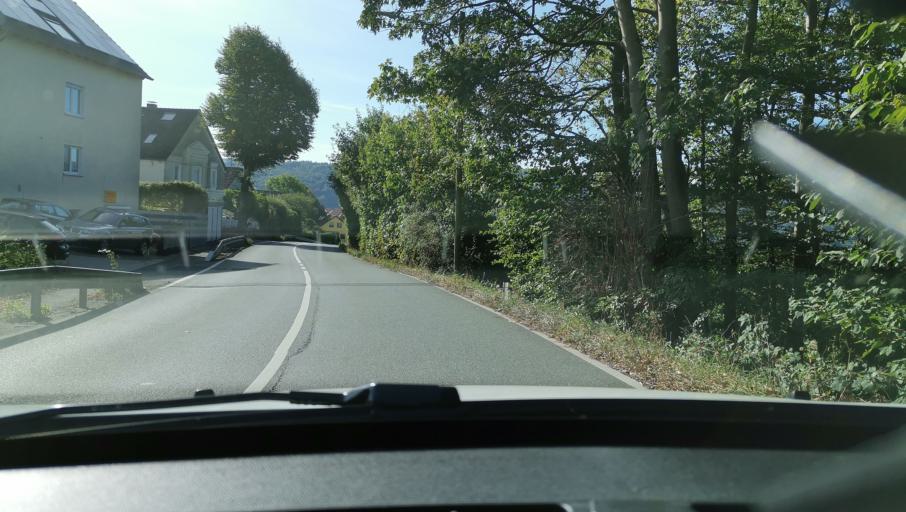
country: DE
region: North Rhine-Westphalia
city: Wetter (Ruhr)
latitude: 51.3456
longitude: 7.3796
